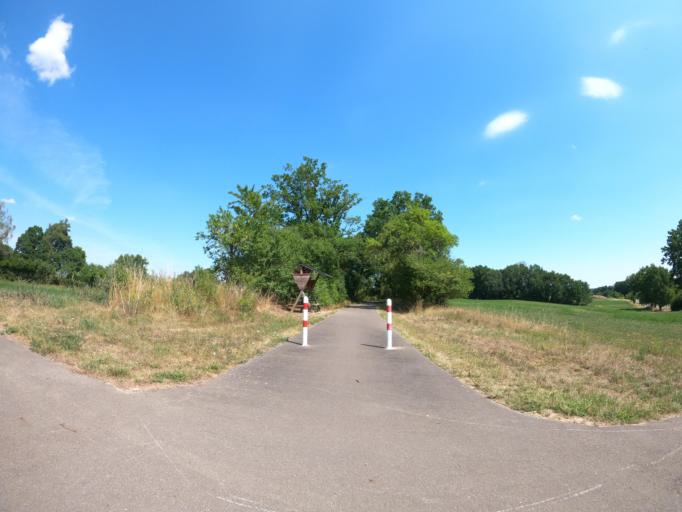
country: DE
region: Brandenburg
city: Templin
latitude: 53.2486
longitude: 13.5066
